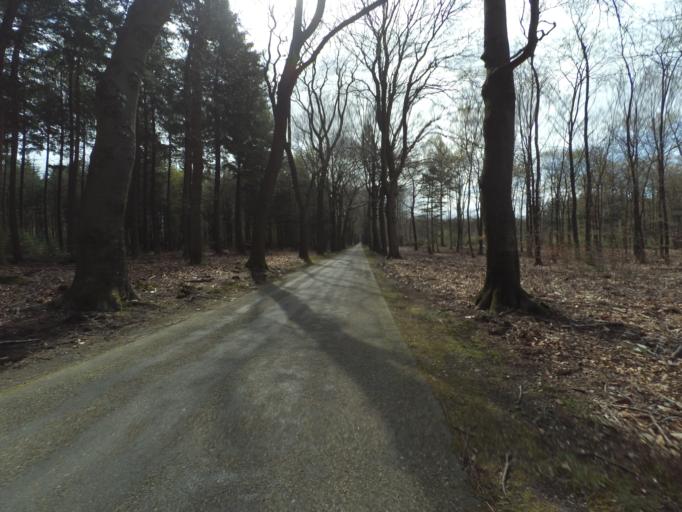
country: NL
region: Gelderland
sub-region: Gemeente Nunspeet
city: Nunspeet
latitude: 52.3571
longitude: 5.8533
